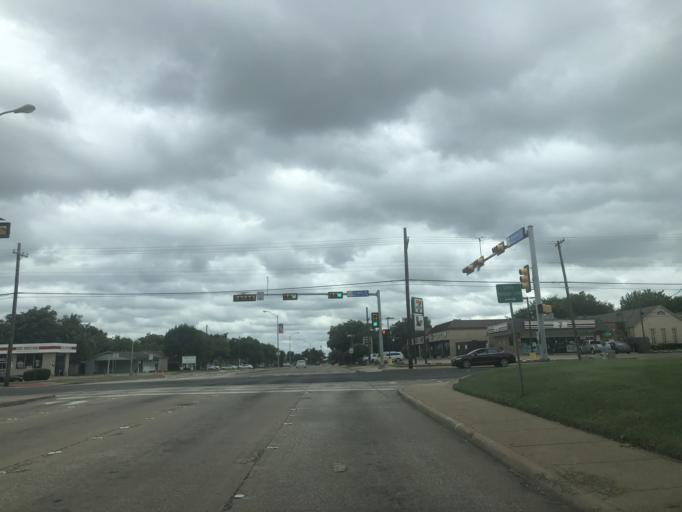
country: US
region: Texas
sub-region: Dallas County
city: Duncanville
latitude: 32.6460
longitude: -96.9080
